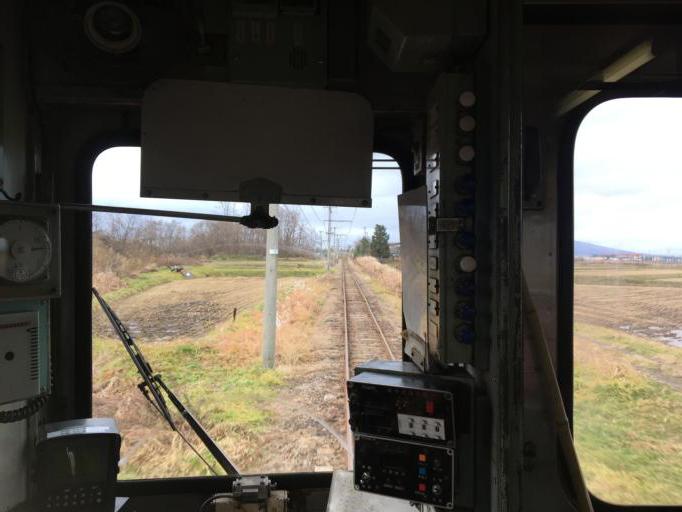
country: JP
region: Aomori
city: Hirosaki
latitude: 40.5611
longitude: 140.4956
